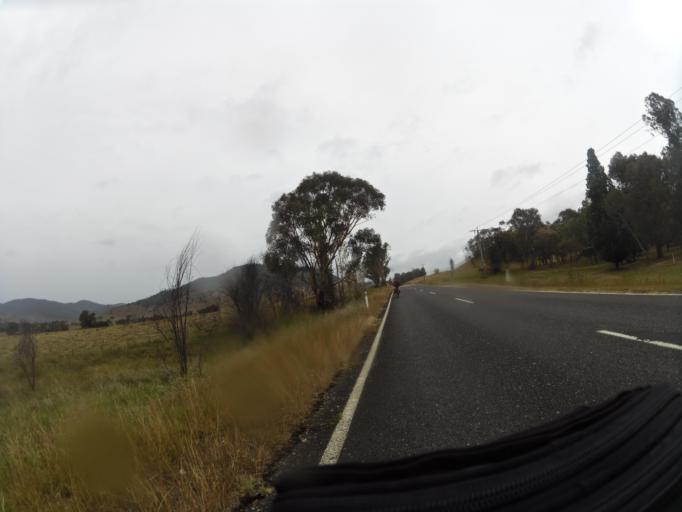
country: AU
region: New South Wales
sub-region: Greater Hume Shire
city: Holbrook
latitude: -36.2122
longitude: 147.7322
